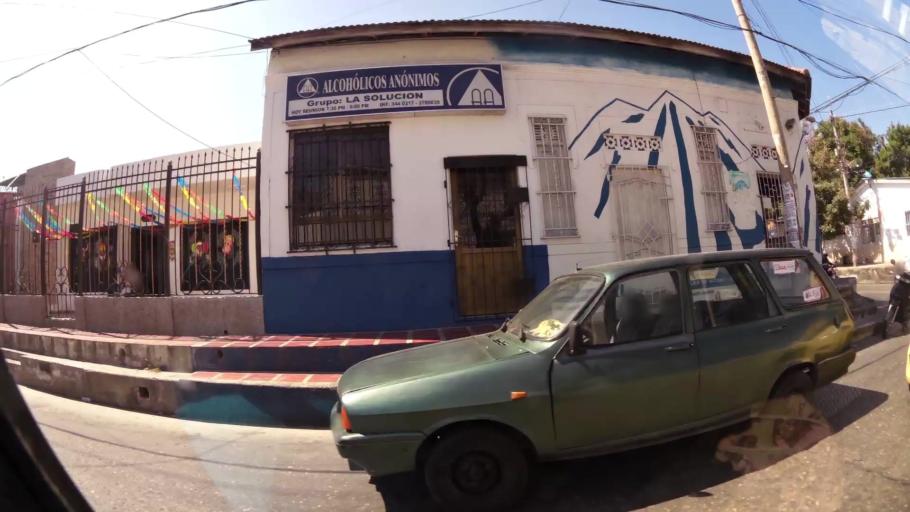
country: CO
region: Atlantico
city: Barranquilla
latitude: 10.9692
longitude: -74.7894
